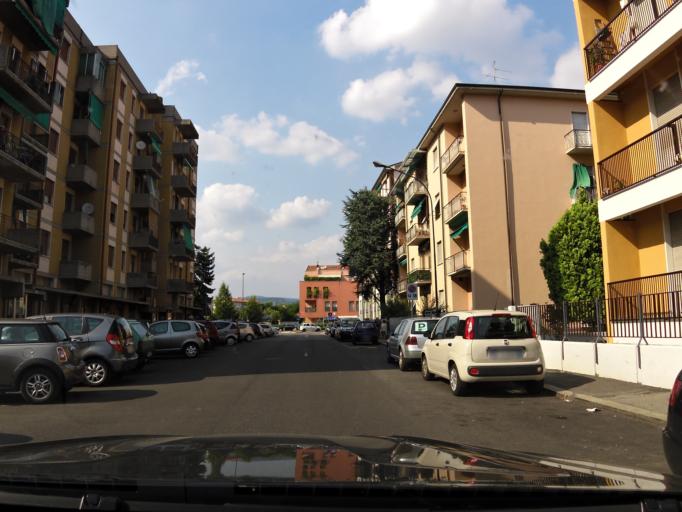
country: IT
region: Veneto
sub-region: Provincia di Verona
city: Verona
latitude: 45.4436
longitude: 10.9634
